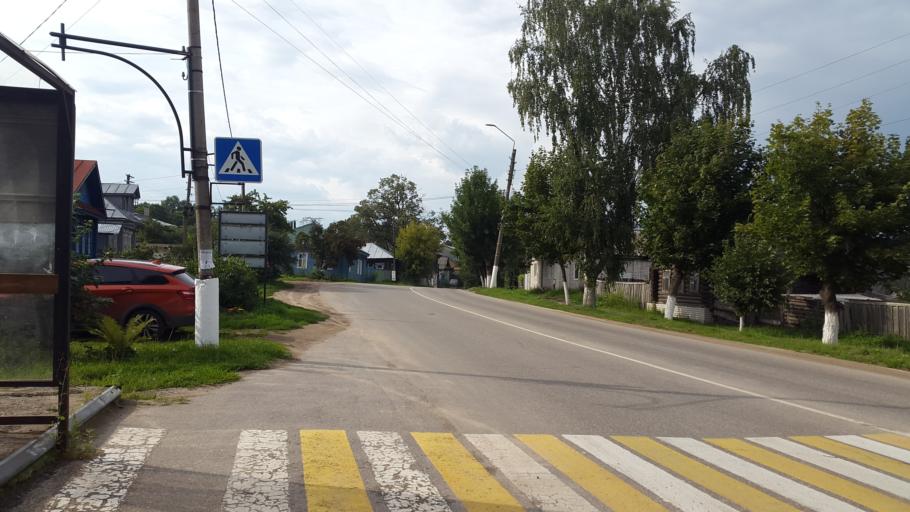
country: RU
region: Vladimir
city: Gorokhovets
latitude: 56.1978
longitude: 42.6929
